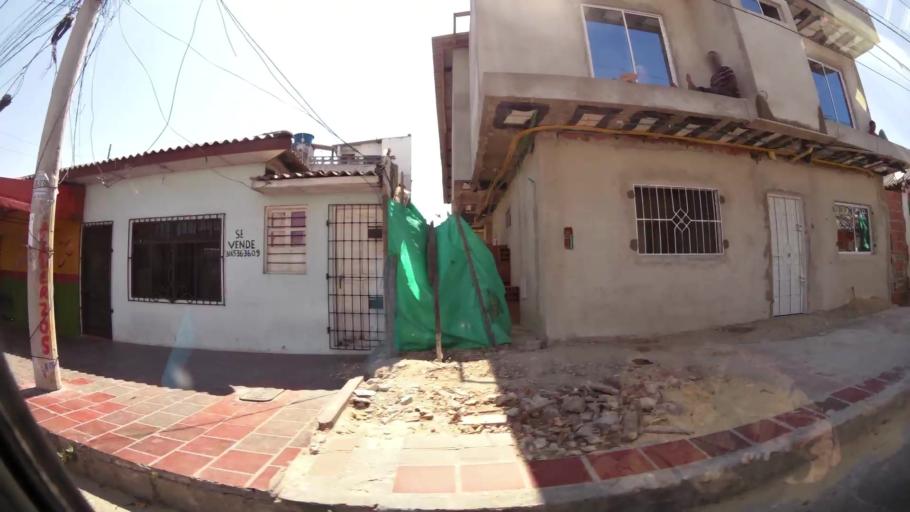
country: CO
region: Atlantico
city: Barranquilla
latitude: 10.9773
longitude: -74.7945
